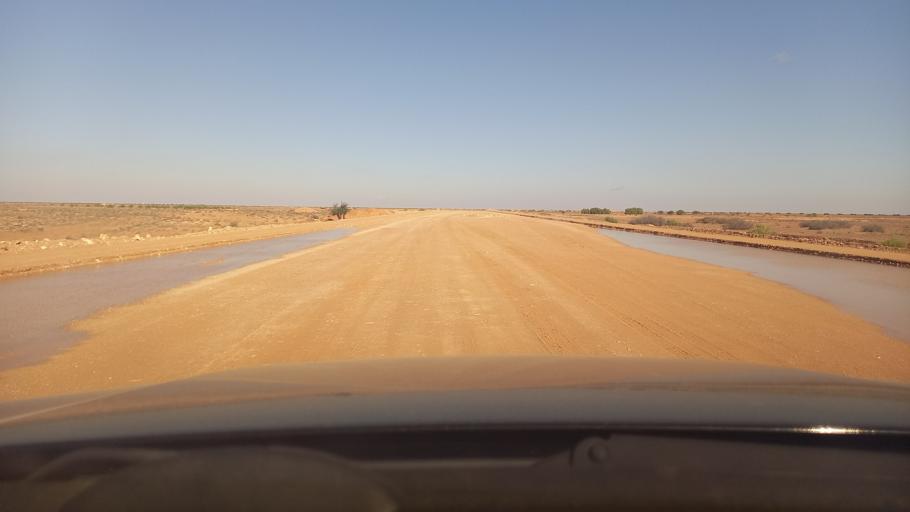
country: TN
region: Tataouine
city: Tataouine
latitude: 33.1385
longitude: 10.5053
